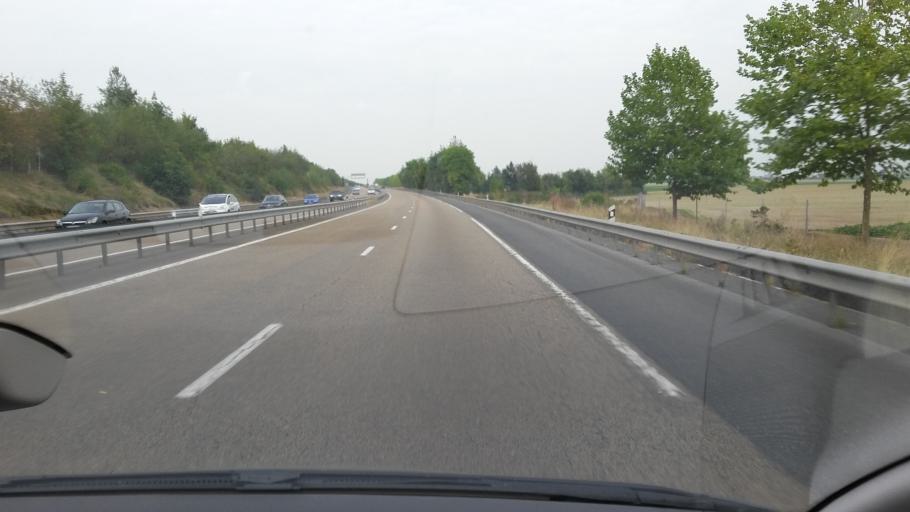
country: FR
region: Champagne-Ardenne
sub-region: Departement de la Marne
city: Witry-les-Reims
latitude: 49.2912
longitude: 4.1276
